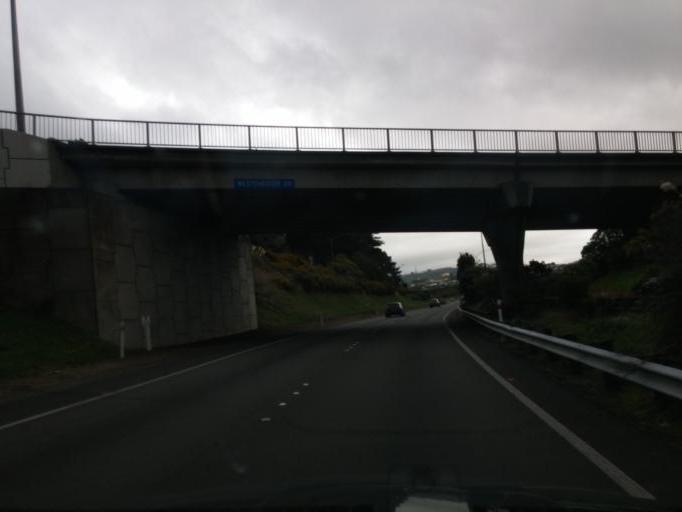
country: NZ
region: Wellington
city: Petone
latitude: -41.2042
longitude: 174.8213
